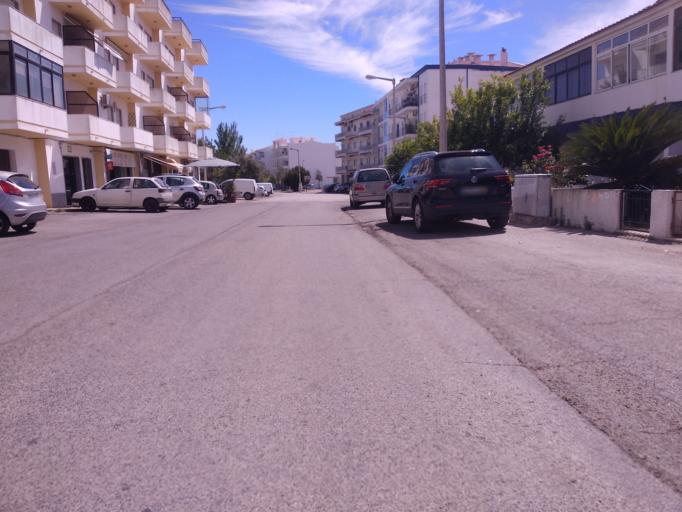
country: PT
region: Faro
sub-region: Sao Bras de Alportel
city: Sao Bras de Alportel
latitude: 37.1562
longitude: -7.8856
